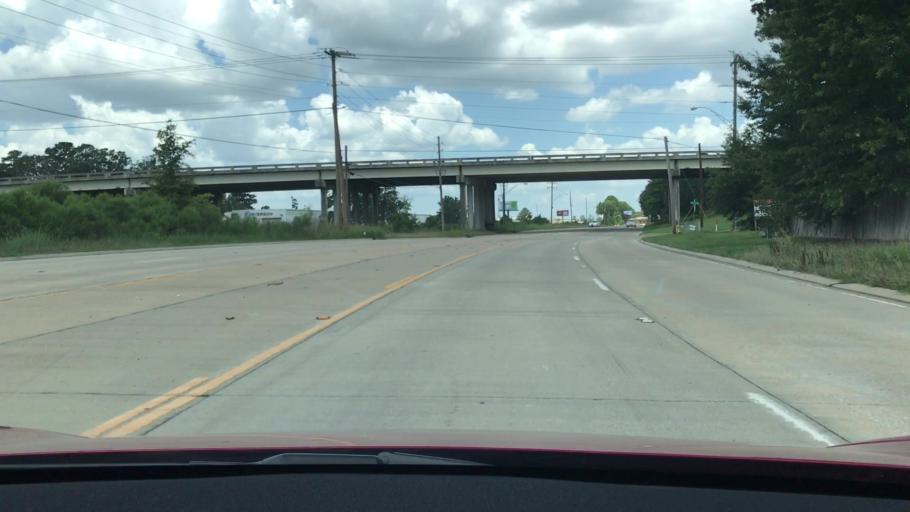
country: US
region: Louisiana
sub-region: Bossier Parish
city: Bossier City
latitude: 32.4000
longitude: -93.7349
